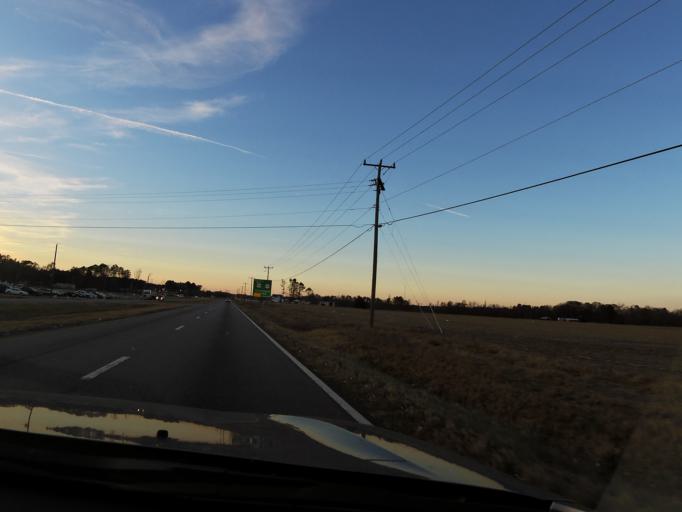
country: US
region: Virginia
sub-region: Southampton County
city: Courtland
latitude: 36.6908
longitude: -77.0291
